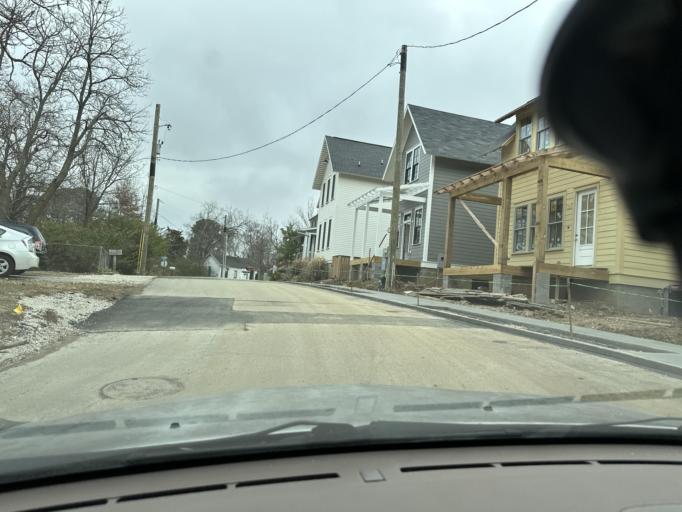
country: US
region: Arkansas
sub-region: Washington County
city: Fayetteville
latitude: 36.0597
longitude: -94.1563
